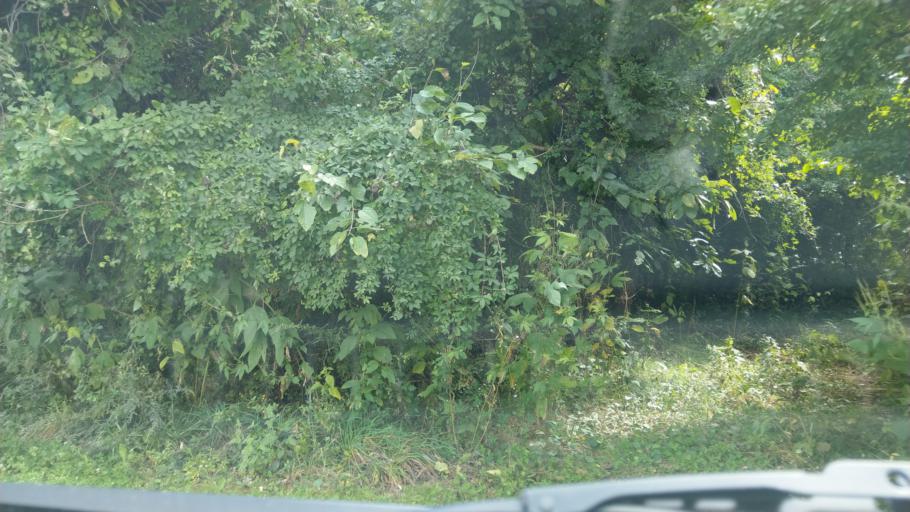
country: JP
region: Nagano
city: Komoro
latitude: 36.3410
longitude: 138.4320
